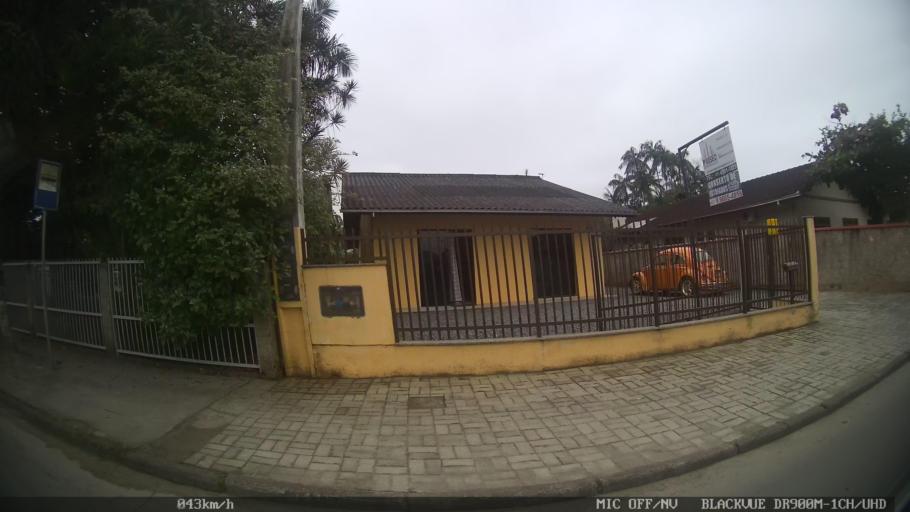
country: BR
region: Santa Catarina
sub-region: Joinville
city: Joinville
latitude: -26.2804
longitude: -48.9070
